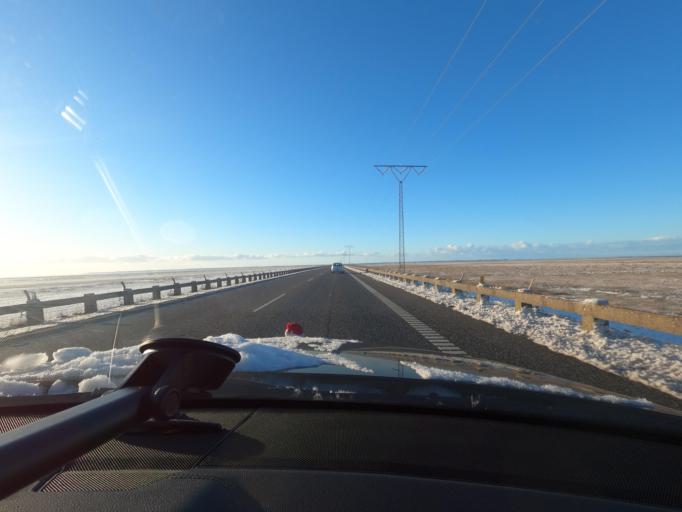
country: DK
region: South Denmark
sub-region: Tonder Kommune
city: Sherrebek
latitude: 55.1520
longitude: 8.6845
